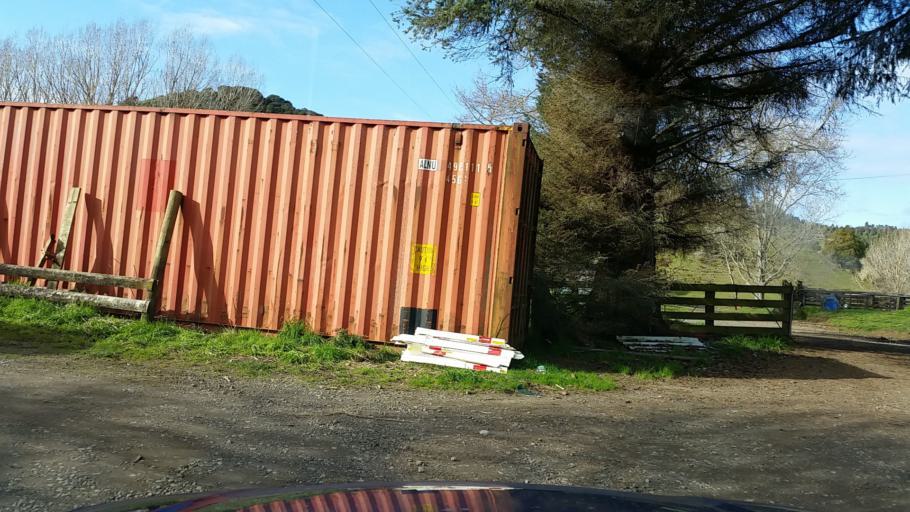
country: NZ
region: Taranaki
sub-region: South Taranaki District
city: Eltham
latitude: -39.2596
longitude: 174.5912
